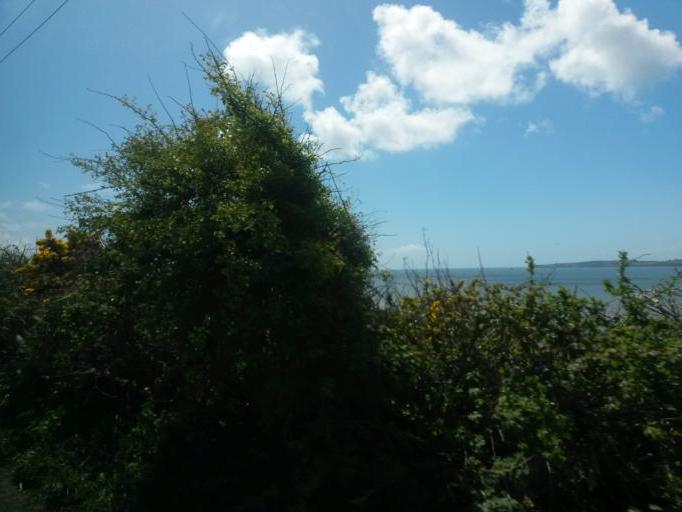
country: IE
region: Munster
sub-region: Waterford
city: Dunmore East
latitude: 52.1734
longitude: -6.8963
